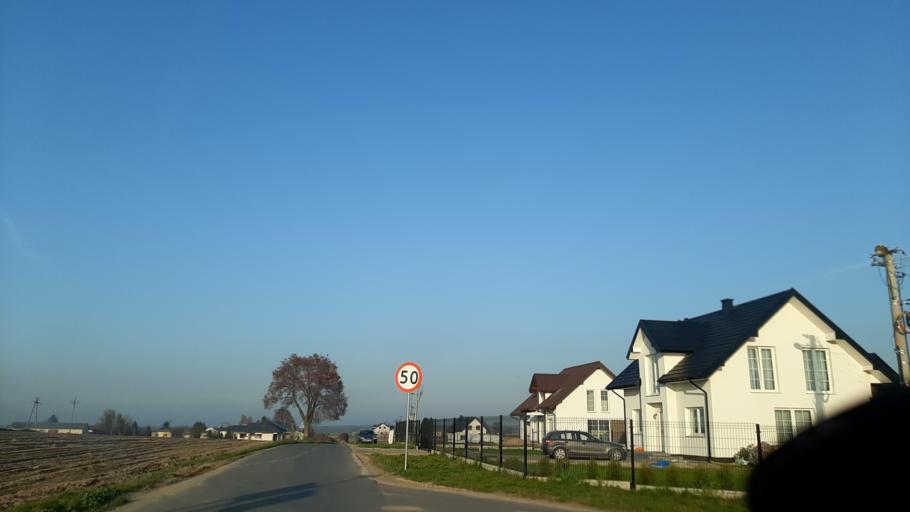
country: PL
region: Lublin Voivodeship
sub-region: Powiat lubelski
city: Garbow
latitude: 51.3844
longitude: 22.3392
